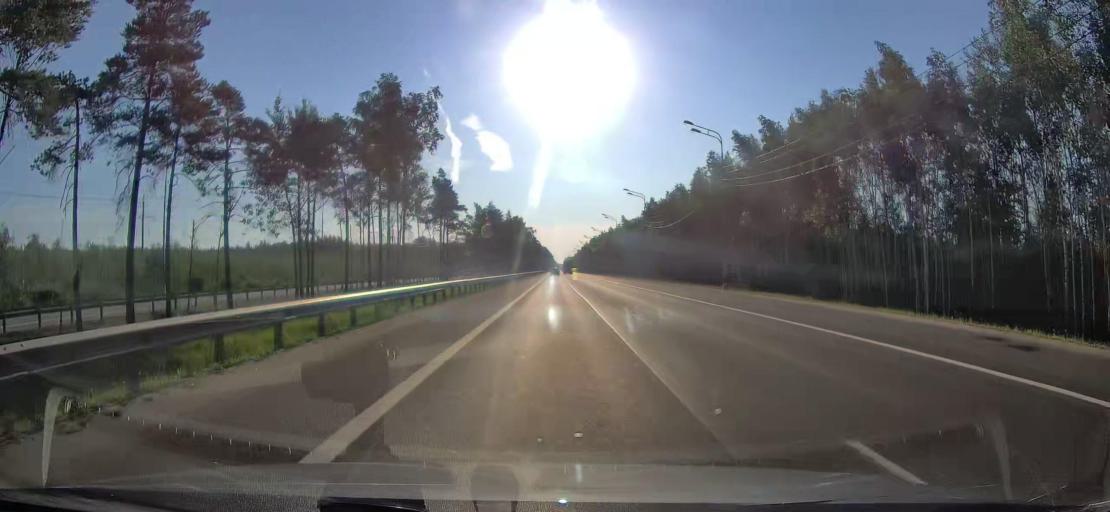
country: RU
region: Leningrad
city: Pavlovo
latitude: 59.9090
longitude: 30.8306
